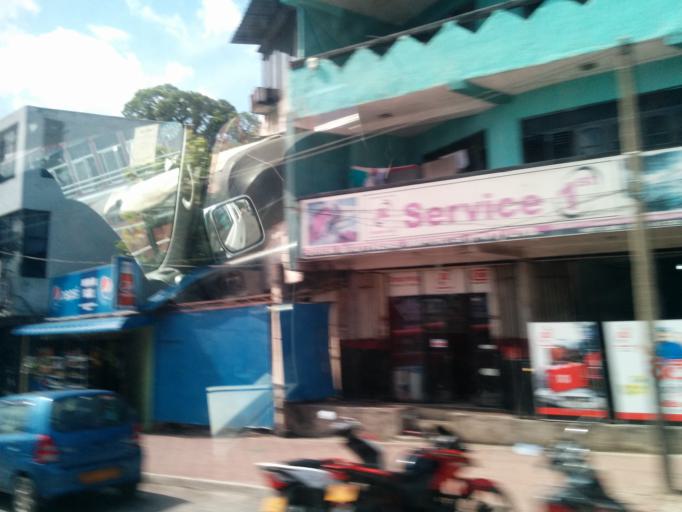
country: LK
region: Western
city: Colombo
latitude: 6.9324
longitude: 79.8616
